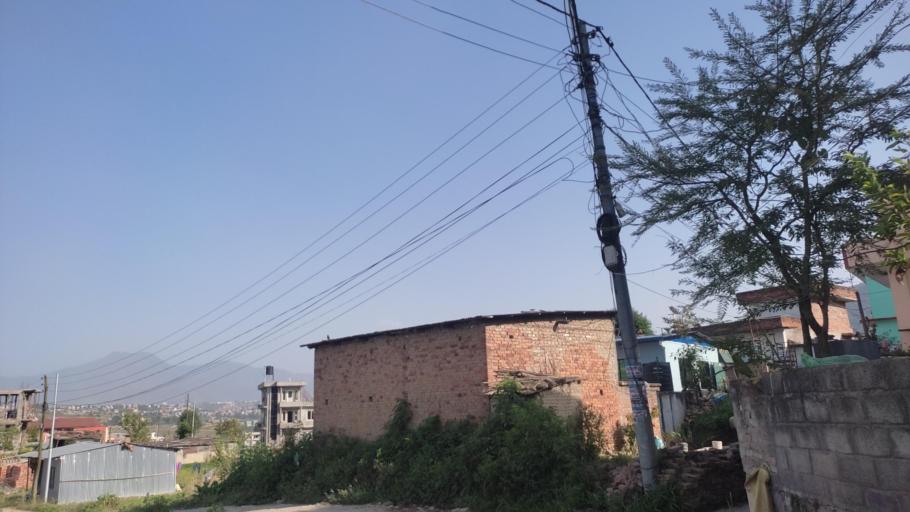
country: NP
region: Central Region
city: Kirtipur
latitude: 27.6529
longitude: 85.2810
